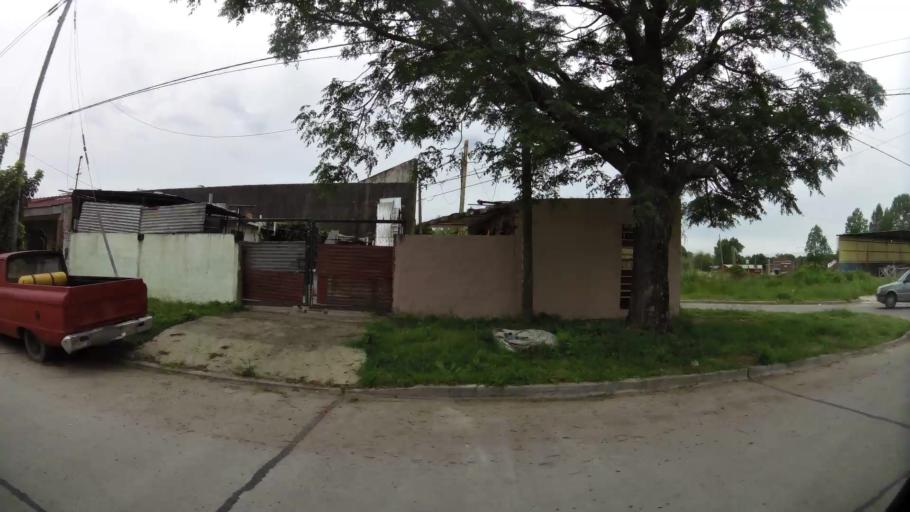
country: AR
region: Buenos Aires
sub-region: Partido de Campana
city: Campana
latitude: -34.1843
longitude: -58.9444
